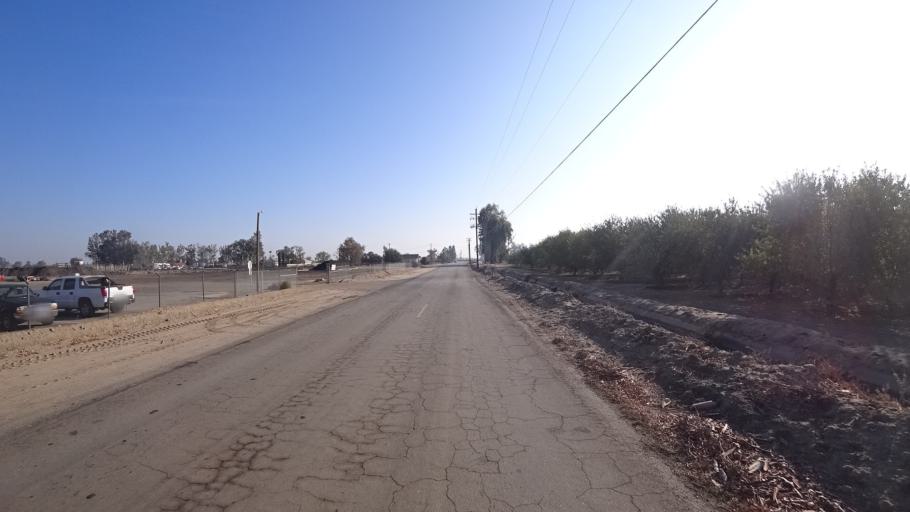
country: US
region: California
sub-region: Kern County
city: Greenfield
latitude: 35.2596
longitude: -119.0274
